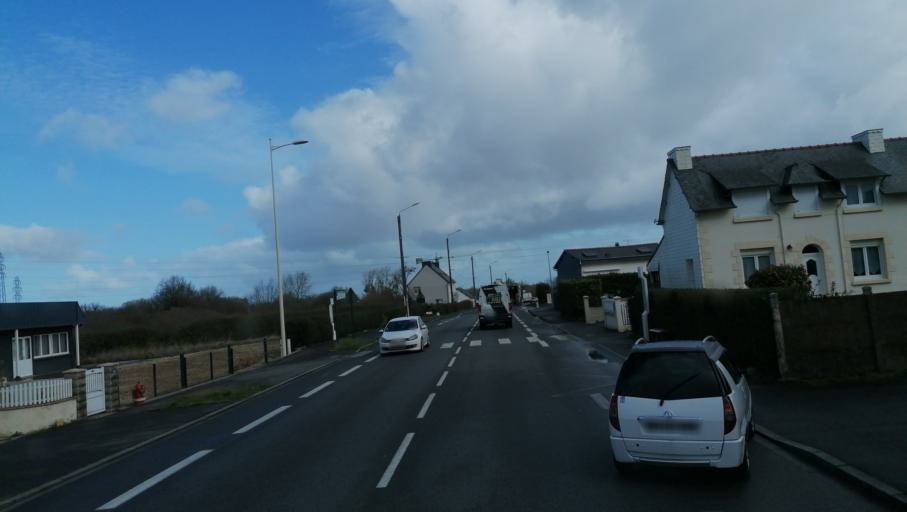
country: FR
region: Brittany
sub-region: Departement des Cotes-d'Armor
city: Ploufragan
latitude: 48.4722
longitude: -2.8017
